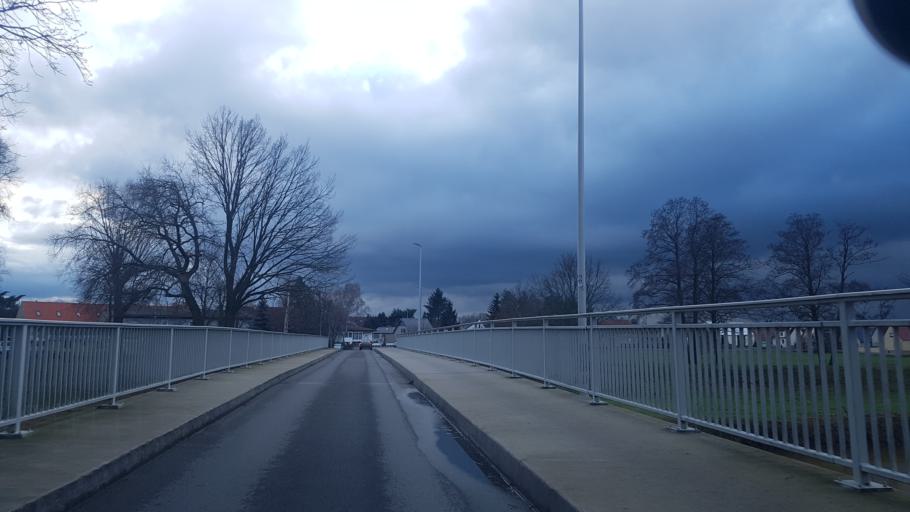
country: DE
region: Brandenburg
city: Elsterwerda
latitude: 51.4531
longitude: 13.5082
